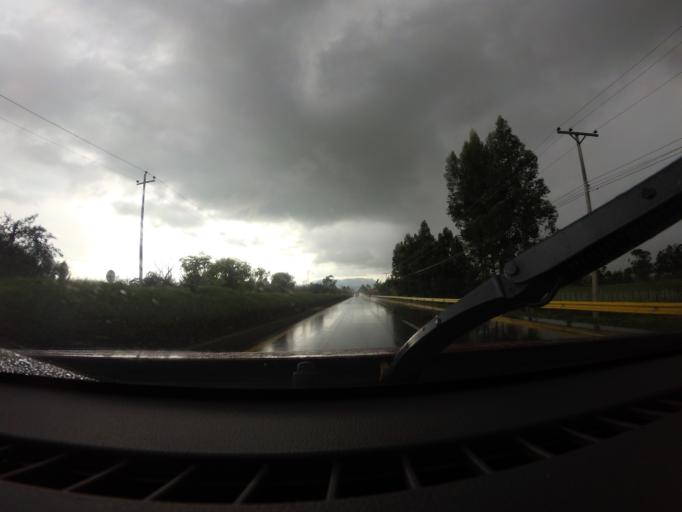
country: CO
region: Cundinamarca
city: El Rosal
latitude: 4.8240
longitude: -74.2357
